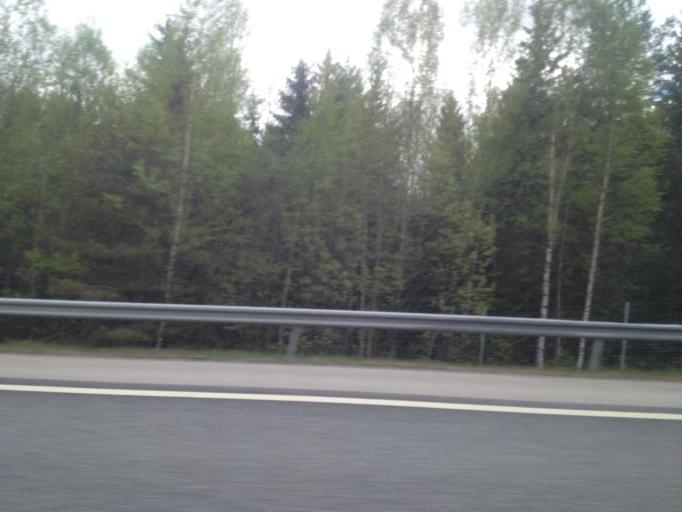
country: FI
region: Haeme
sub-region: Haemeenlinna
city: Haemeenlinna
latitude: 60.9441
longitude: 24.5099
